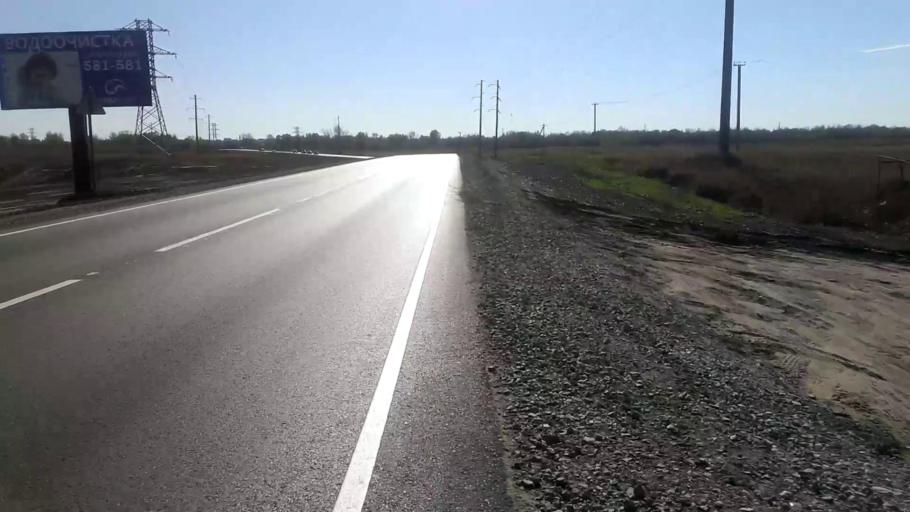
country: RU
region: Altai Krai
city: Sannikovo
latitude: 53.3346
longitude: 83.9381
